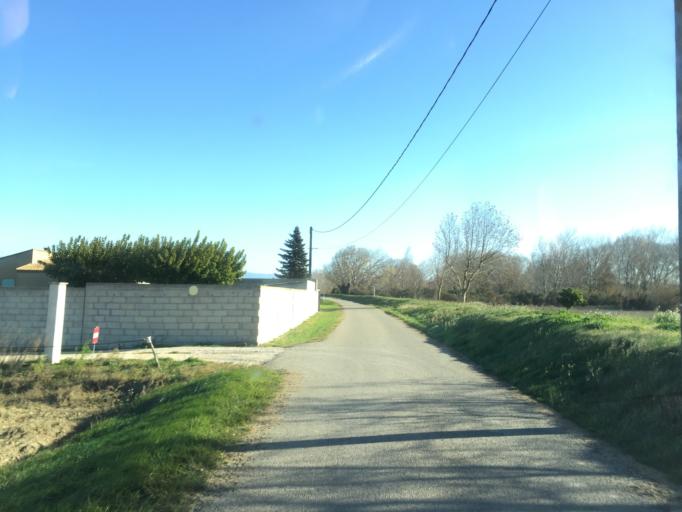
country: FR
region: Provence-Alpes-Cote d'Azur
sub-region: Departement du Vaucluse
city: Bedarrides
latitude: 44.0397
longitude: 4.9141
